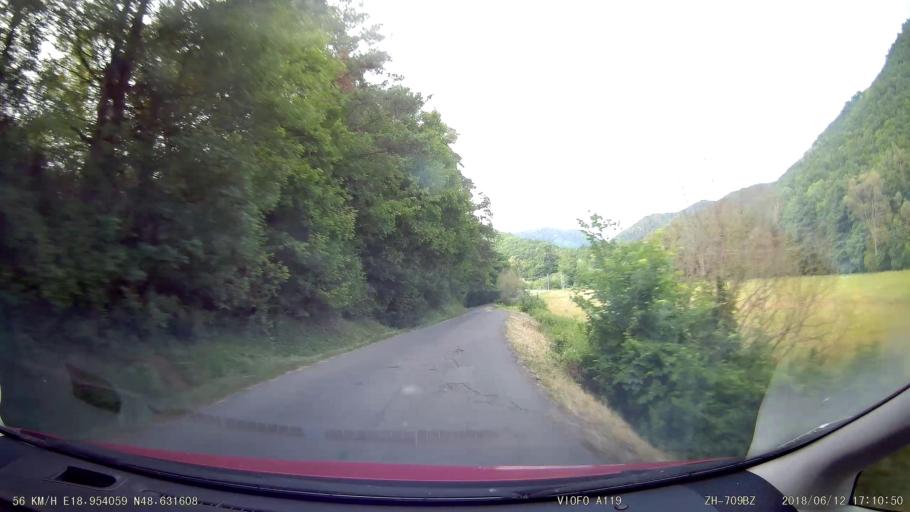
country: SK
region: Banskobystricky
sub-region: Okres Ziar nad Hronom
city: Kremnica
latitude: 48.6319
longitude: 18.9542
